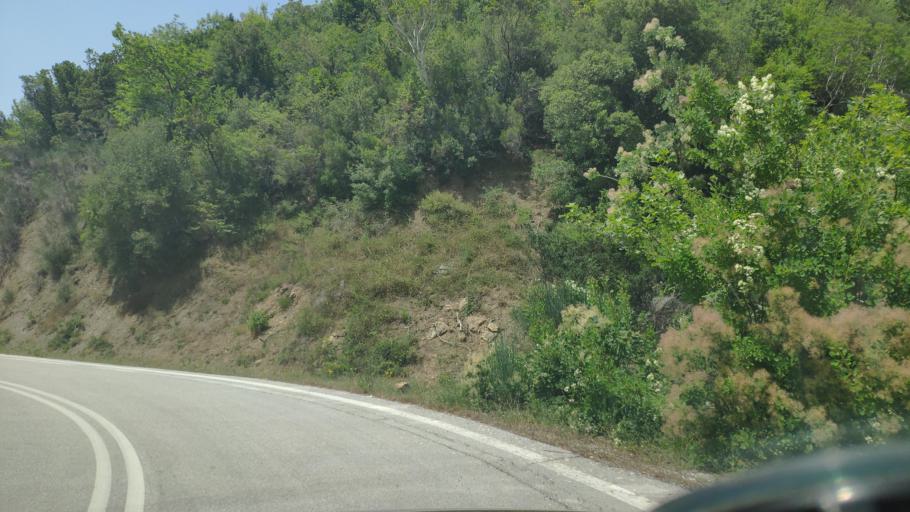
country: GR
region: Thessaly
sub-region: Nomos Kardhitsas
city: Anthiro
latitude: 39.2660
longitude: 21.3438
